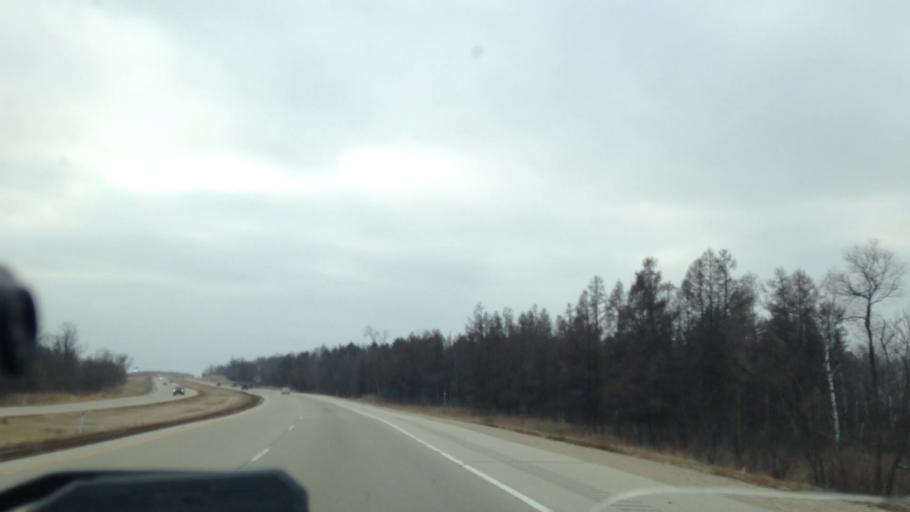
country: US
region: Wisconsin
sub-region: Washington County
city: Jackson
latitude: 43.3707
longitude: -88.1943
